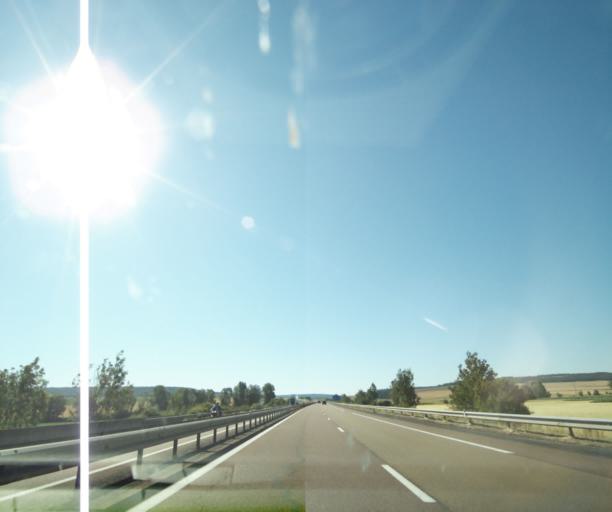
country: FR
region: Champagne-Ardenne
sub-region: Departement de l'Aube
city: Ville-sous-la-Ferte
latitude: 48.1103
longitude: 4.7882
